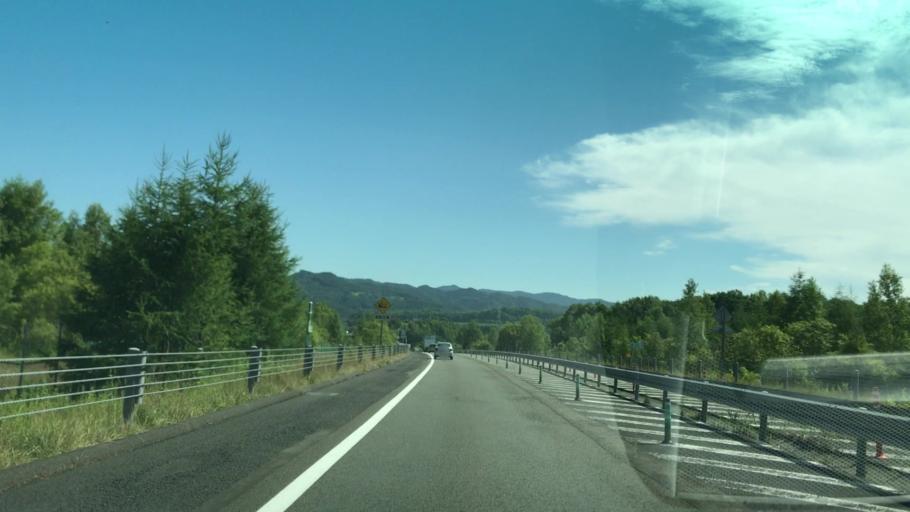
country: JP
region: Hokkaido
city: Chitose
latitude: 42.9013
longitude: 141.8894
